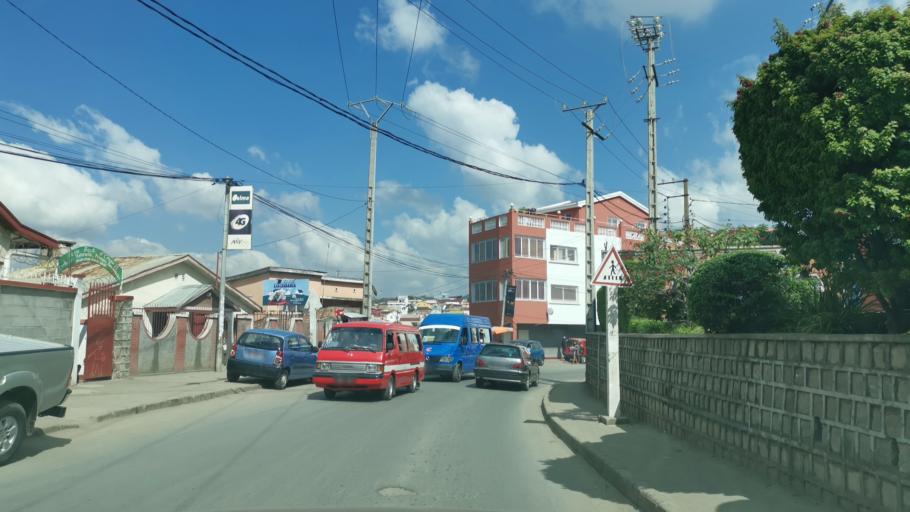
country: MG
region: Analamanga
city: Antananarivo
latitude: -18.9356
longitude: 47.5304
